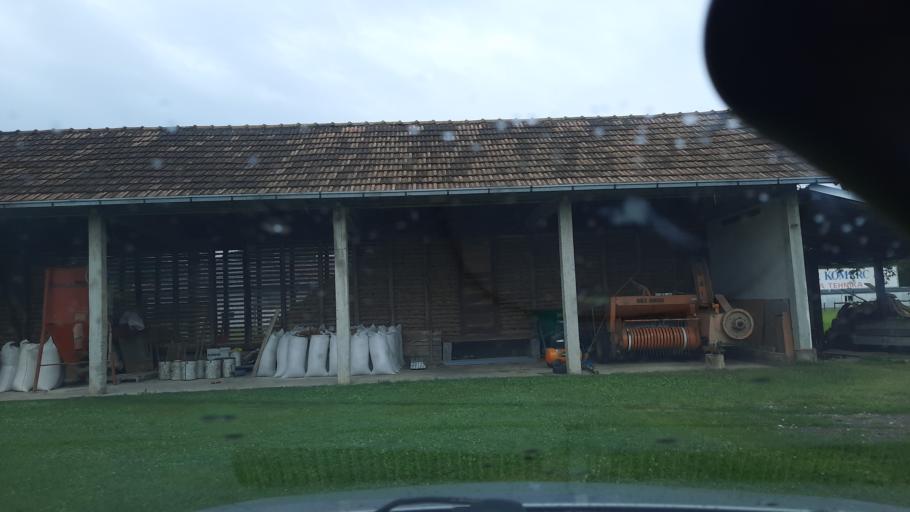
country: RS
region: Central Serbia
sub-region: Raski Okrug
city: Vrnjacka Banja
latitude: 43.7103
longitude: 20.8361
